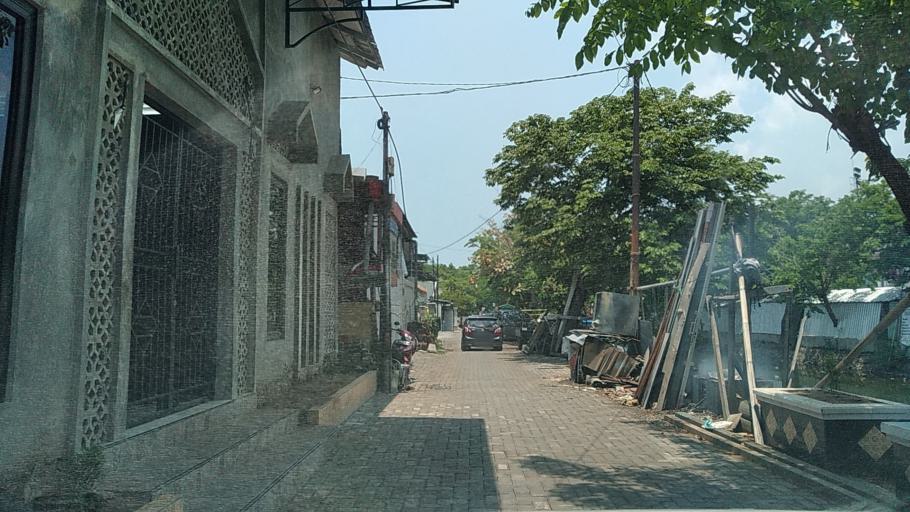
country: ID
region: Central Java
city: Semarang
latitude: -6.9714
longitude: 110.4383
